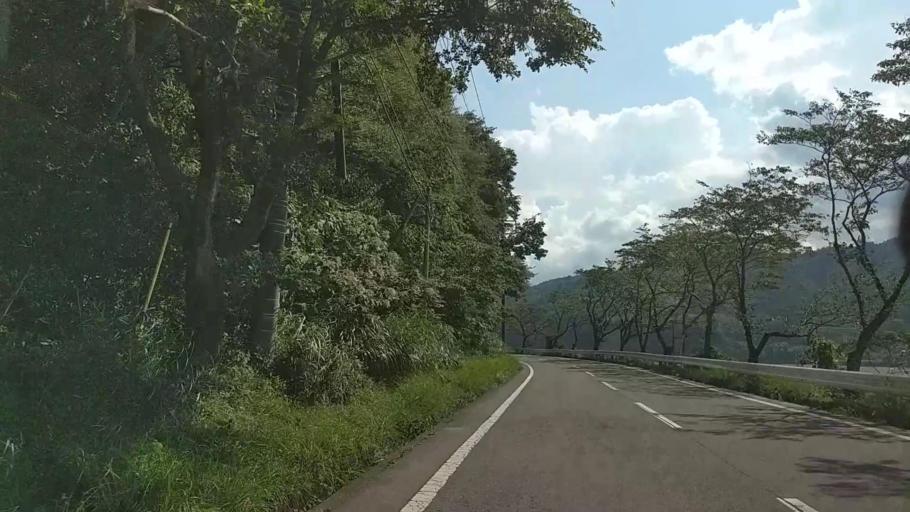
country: JP
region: Shizuoka
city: Fujinomiya
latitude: 35.3971
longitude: 138.4495
